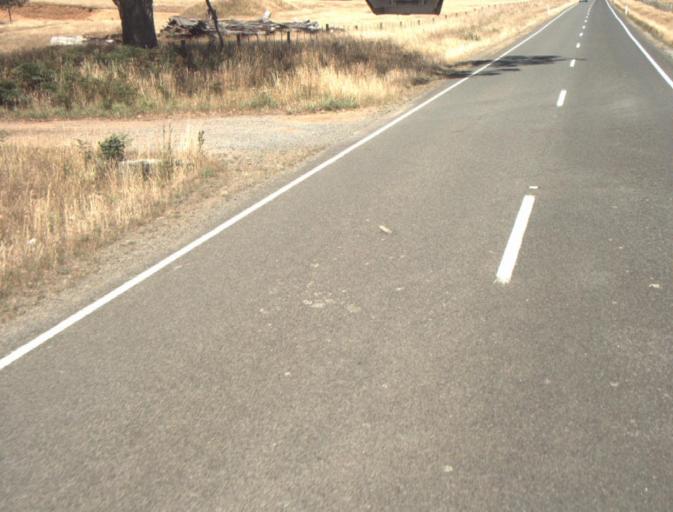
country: AU
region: Tasmania
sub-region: Dorset
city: Scottsdale
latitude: -41.2892
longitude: 147.3846
